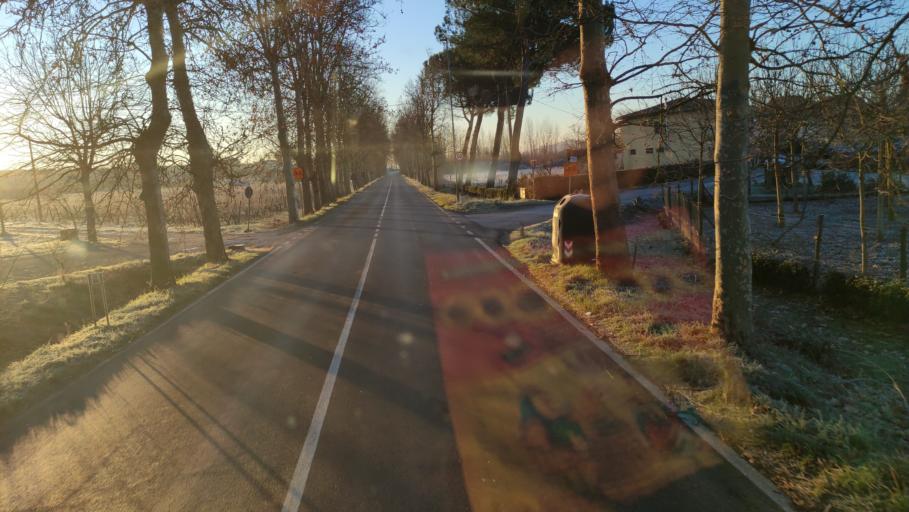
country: IT
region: Tuscany
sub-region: Province of Pisa
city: Ponte A Elsa
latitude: 43.6661
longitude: 10.9274
